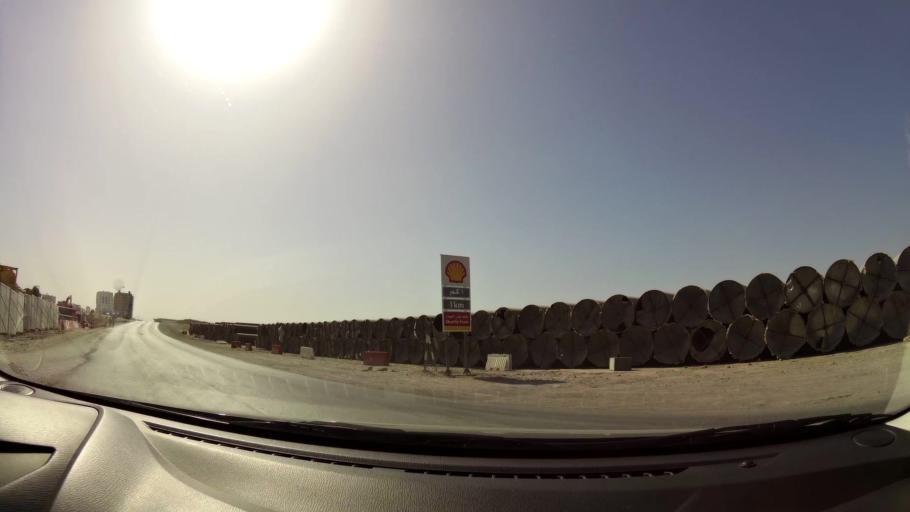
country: OM
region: Muhafazat Masqat
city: Bawshar
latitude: 23.5798
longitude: 58.3626
